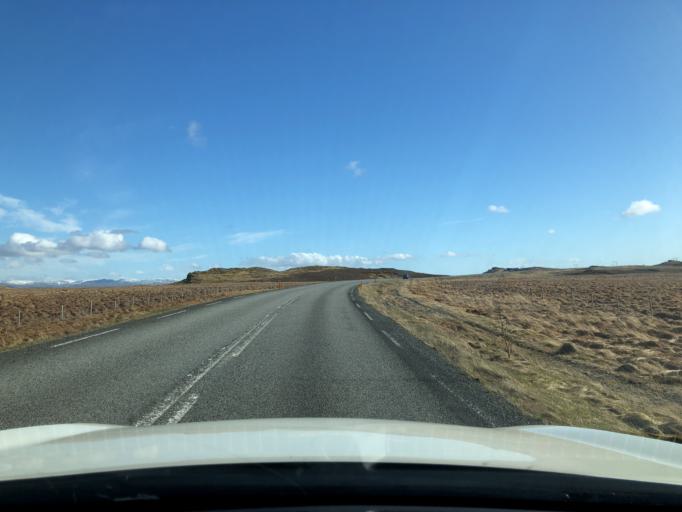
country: IS
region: West
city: Borgarnes
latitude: 64.5568
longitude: -21.7309
